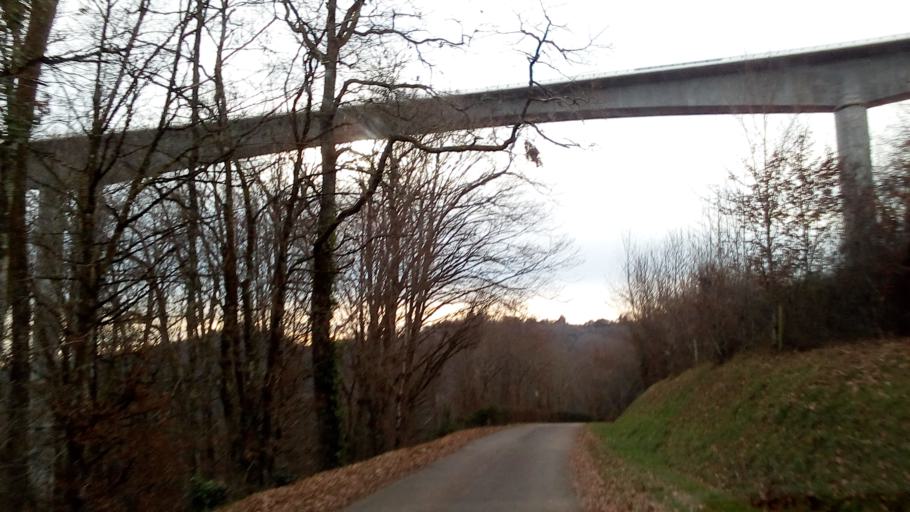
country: FR
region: Limousin
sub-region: Departement de la Correze
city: Naves
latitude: 45.3190
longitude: 1.7896
